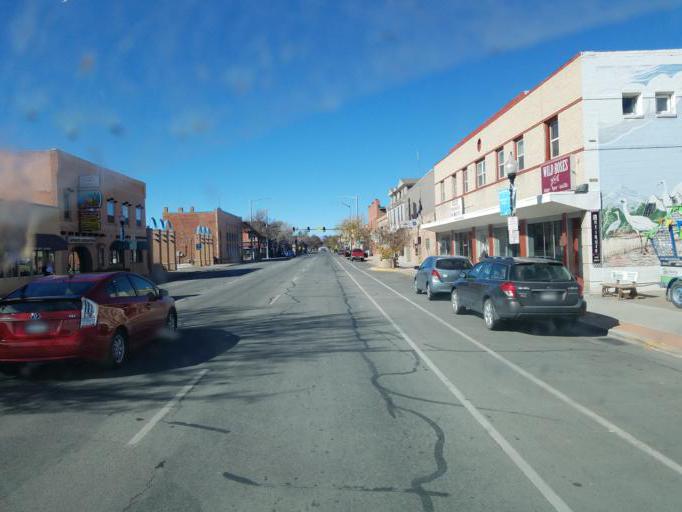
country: US
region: Colorado
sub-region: Alamosa County
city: Alamosa
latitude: 37.4683
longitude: -105.8641
